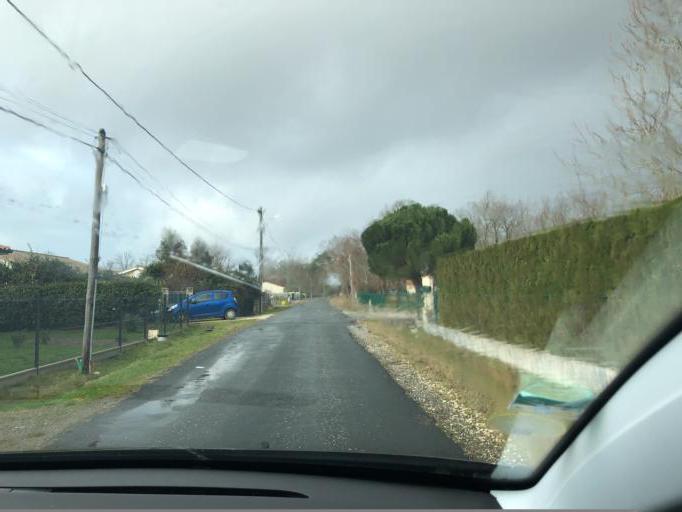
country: FR
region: Aquitaine
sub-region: Departement de la Gironde
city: Hourtin
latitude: 45.1794
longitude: -1.0527
